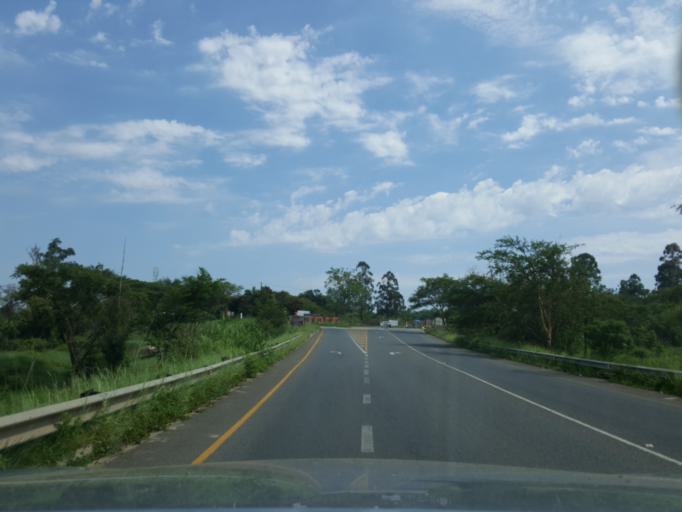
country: ZA
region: Mpumalanga
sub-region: Ehlanzeni District
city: White River
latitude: -25.3552
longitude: 31.0714
